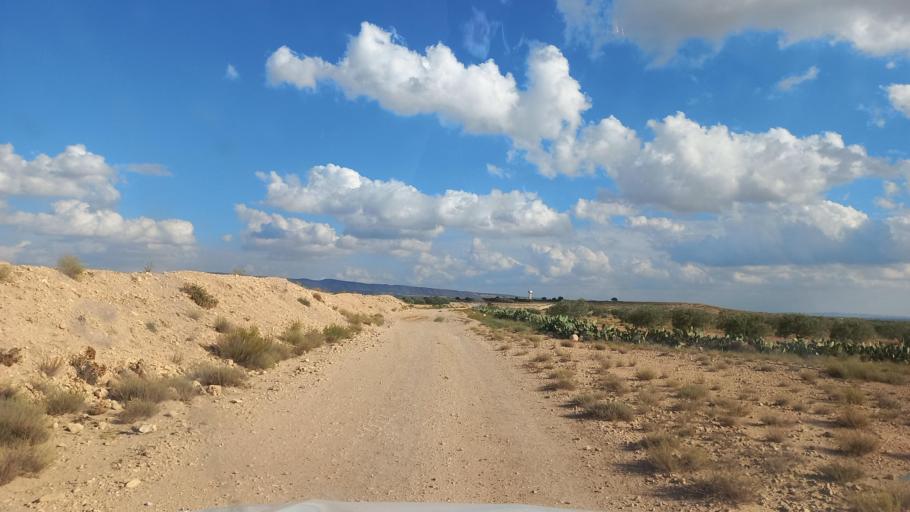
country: TN
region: Al Qasrayn
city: Sbiba
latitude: 35.3978
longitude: 9.0371
